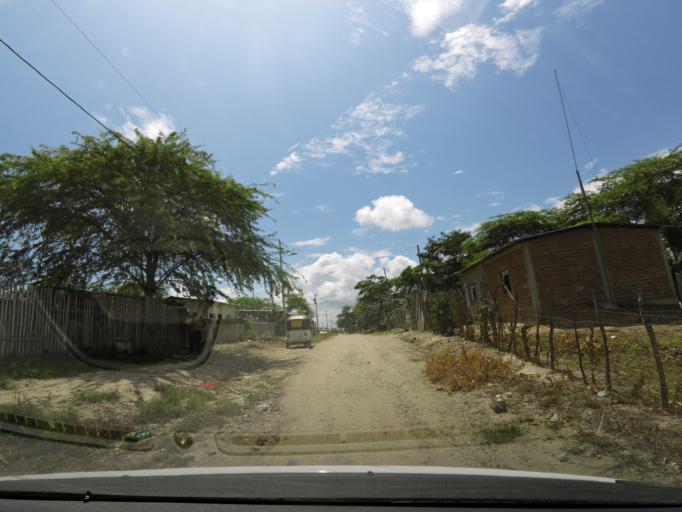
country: EC
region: El Oro
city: Huaquillas
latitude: -3.4730
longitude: -80.2127
